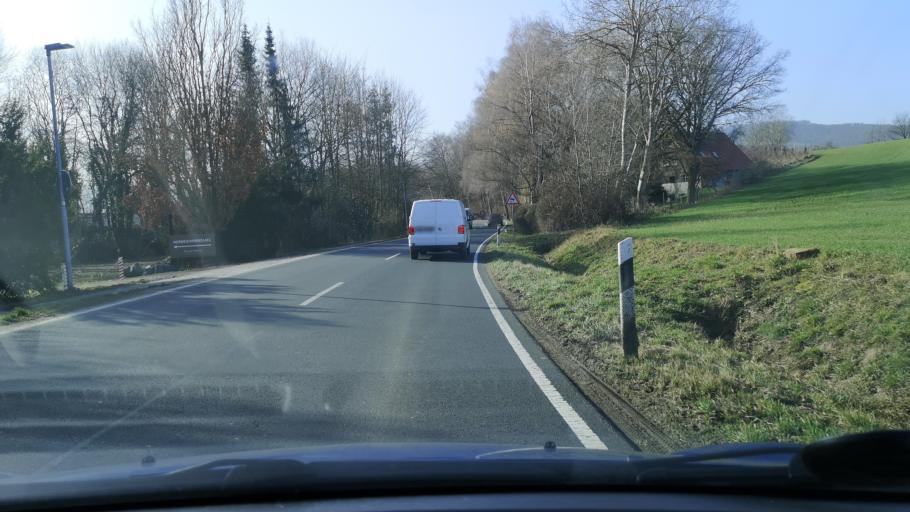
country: DE
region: Lower Saxony
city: Salzhemmendorf
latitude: 52.0733
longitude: 9.5872
